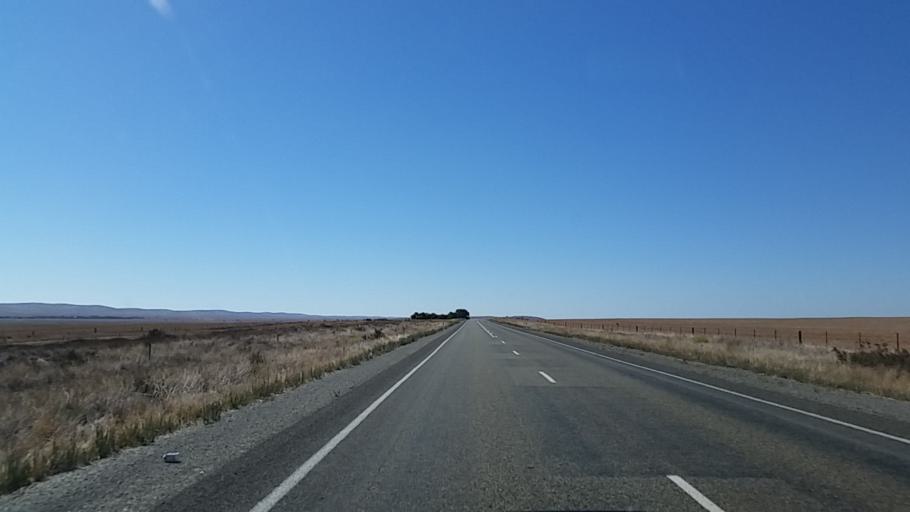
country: AU
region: South Australia
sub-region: Northern Areas
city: Jamestown
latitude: -33.2634
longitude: 138.8694
